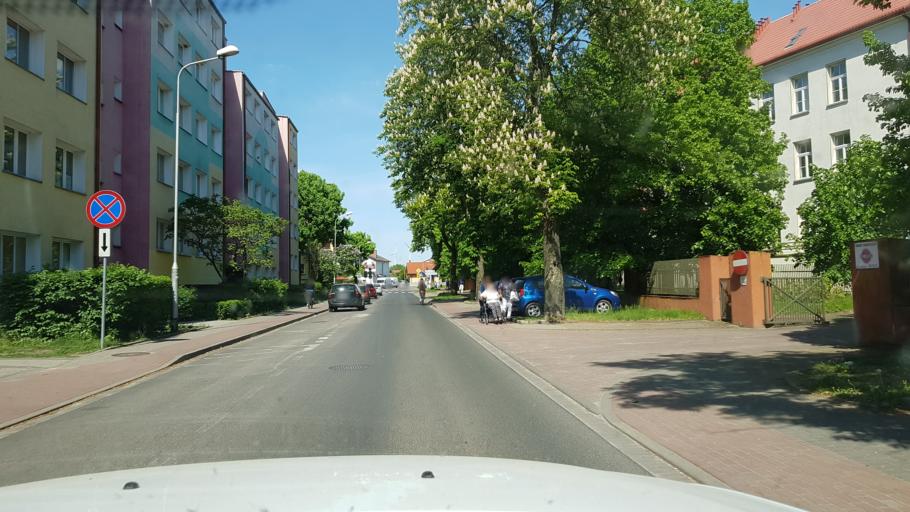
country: PL
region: West Pomeranian Voivodeship
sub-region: Powiat bialogardzki
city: Bialogard
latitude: 54.0065
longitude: 16.0062
